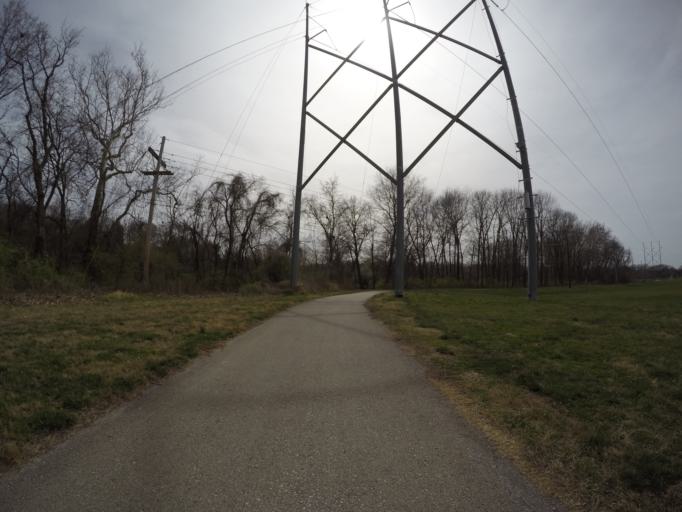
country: US
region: Kansas
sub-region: Johnson County
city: Leawood
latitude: 38.9314
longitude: -94.6136
